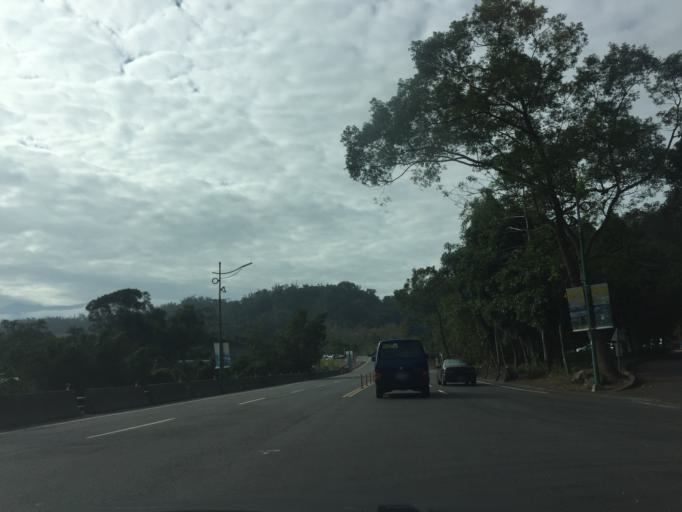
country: TW
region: Taiwan
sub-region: Nantou
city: Puli
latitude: 23.8535
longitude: 120.9016
